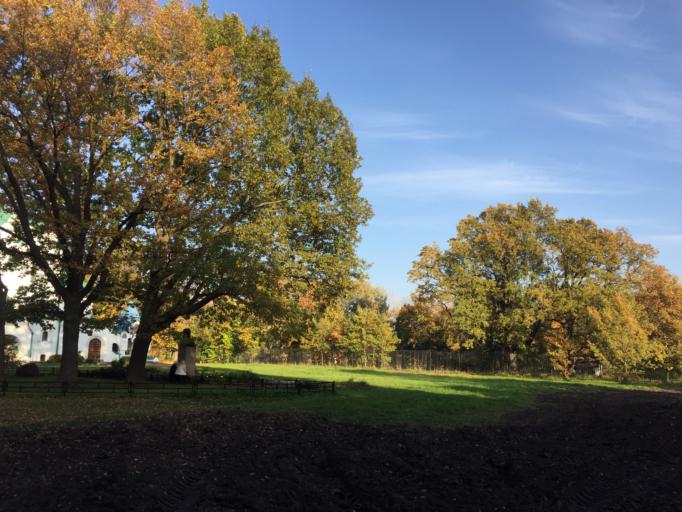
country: RU
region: St.-Petersburg
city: Pushkin
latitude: 59.7253
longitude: 30.3896
